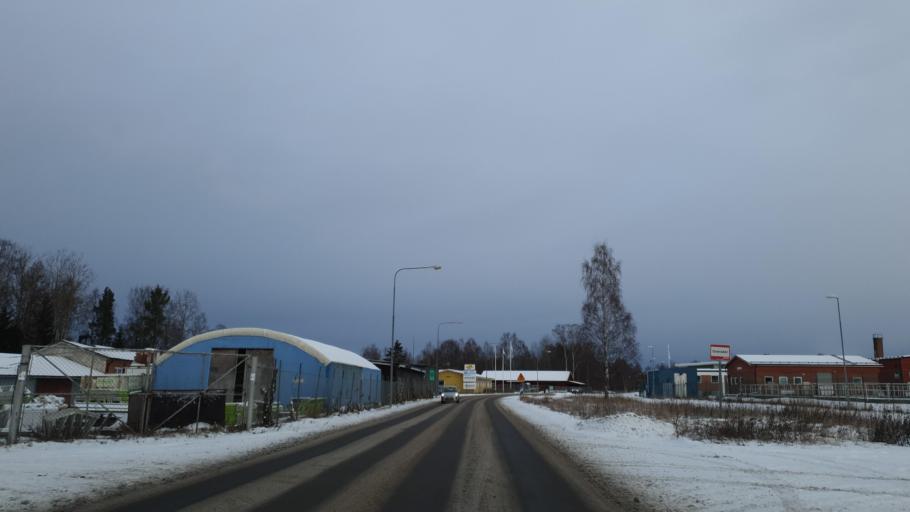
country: SE
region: Gaevleborg
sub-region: Soderhamns Kommun
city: Soderhamn
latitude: 61.3106
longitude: 17.0746
